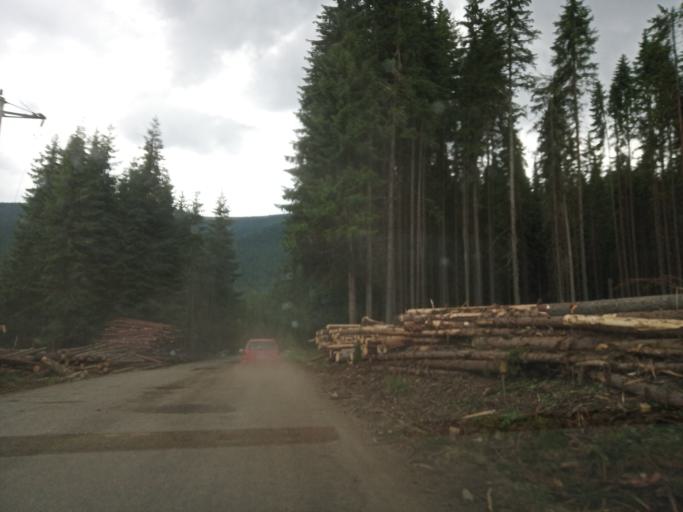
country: RO
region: Valcea
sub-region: Comuna Voineasa
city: Voineasa
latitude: 45.4158
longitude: 23.7232
